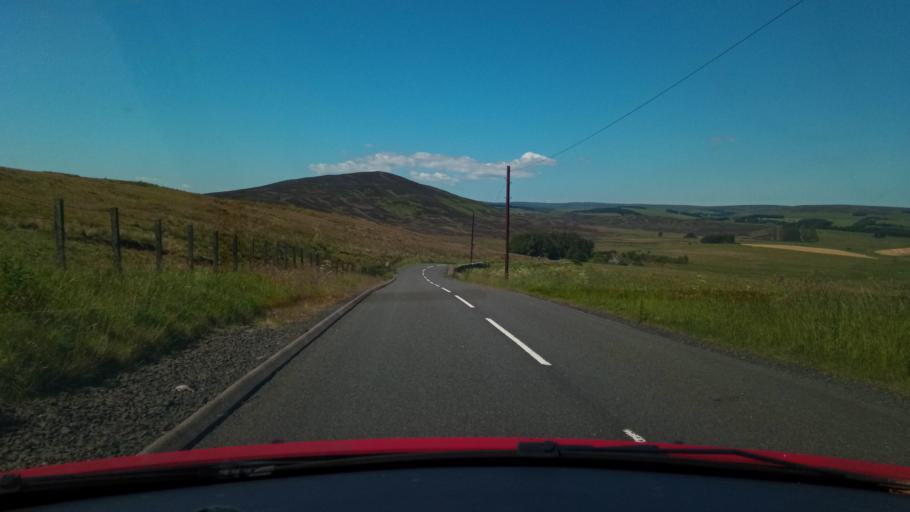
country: GB
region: Scotland
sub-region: The Scottish Borders
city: Duns
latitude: 55.7832
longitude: -2.4450
